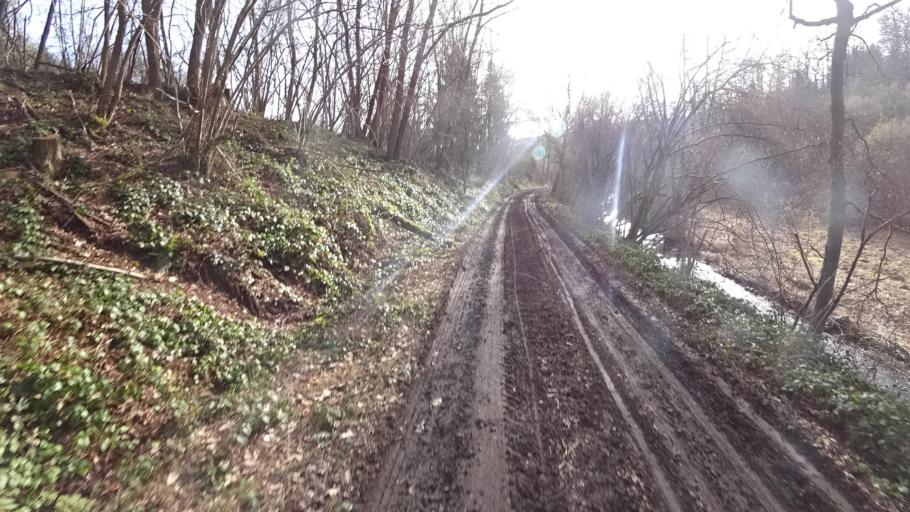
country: DE
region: Rheinland-Pfalz
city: Scheuerfeld
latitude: 50.7719
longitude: 7.8349
